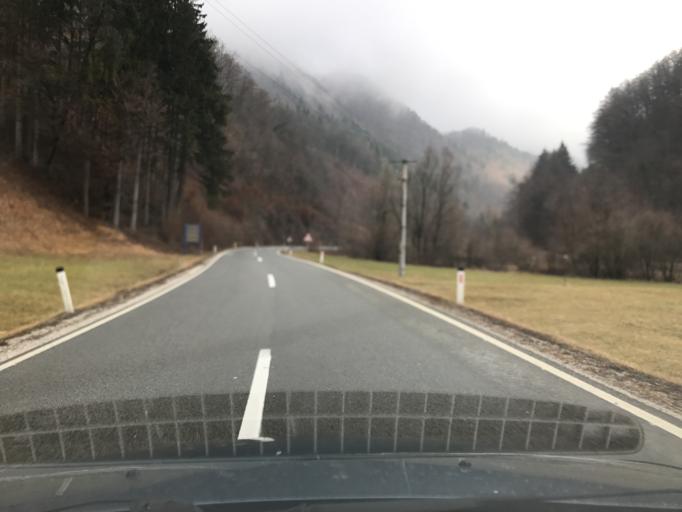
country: SI
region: Vransko
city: Vransko
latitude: 46.2199
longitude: 14.9115
